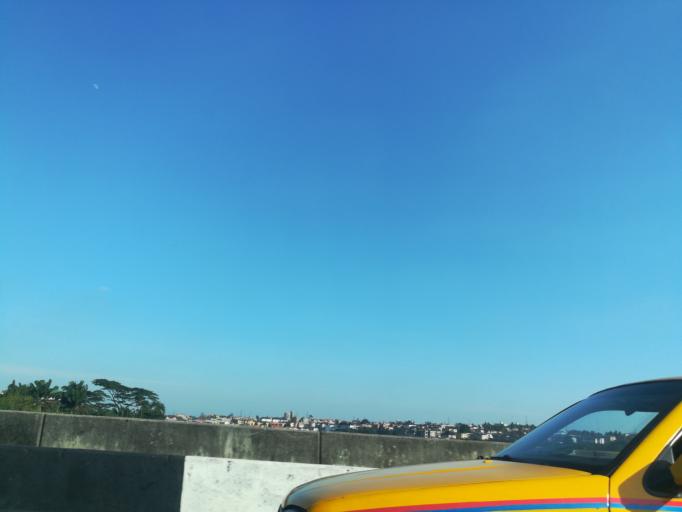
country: NG
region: Lagos
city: Ojota
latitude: 6.5852
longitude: 3.3628
